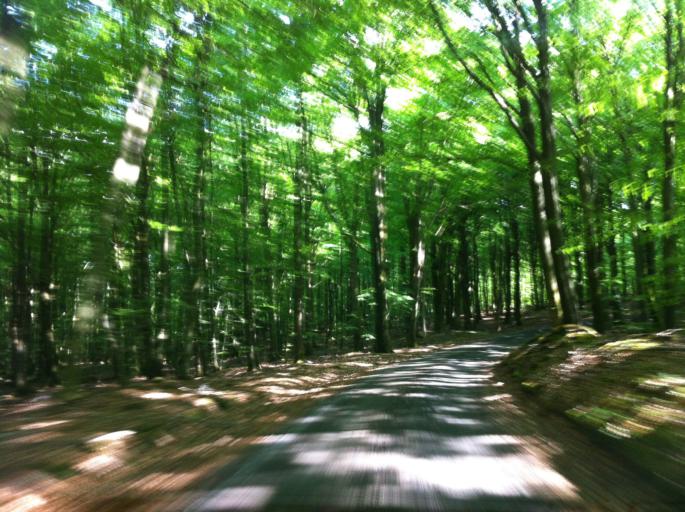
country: SE
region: Skane
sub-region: Klippans Kommun
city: Ljungbyhed
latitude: 56.0461
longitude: 13.2217
